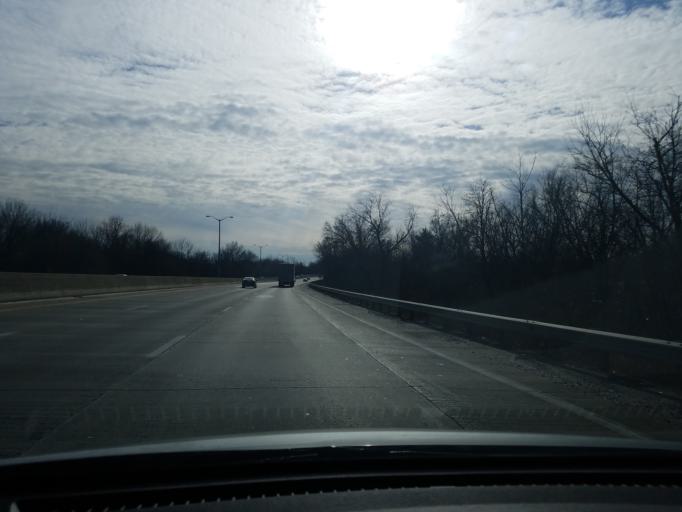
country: US
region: Kentucky
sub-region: Jefferson County
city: Shively
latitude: 38.2017
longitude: -85.8275
